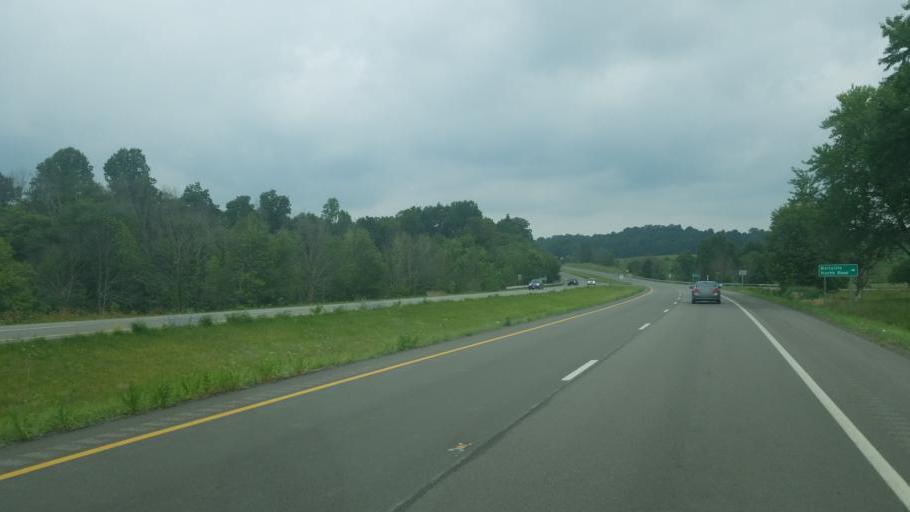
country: US
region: Ohio
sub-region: Sandusky County
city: Bellville
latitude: 40.6576
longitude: -82.5133
